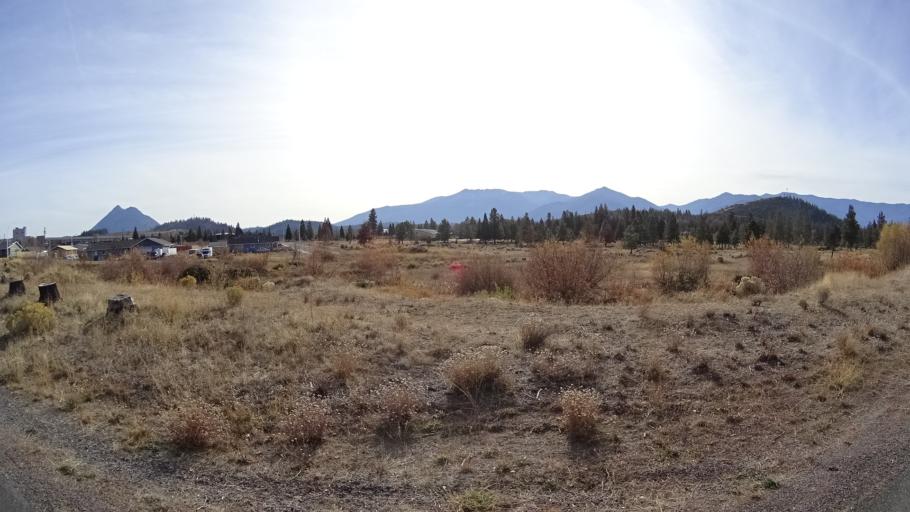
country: US
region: California
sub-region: Siskiyou County
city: Weed
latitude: 41.4395
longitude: -122.3823
